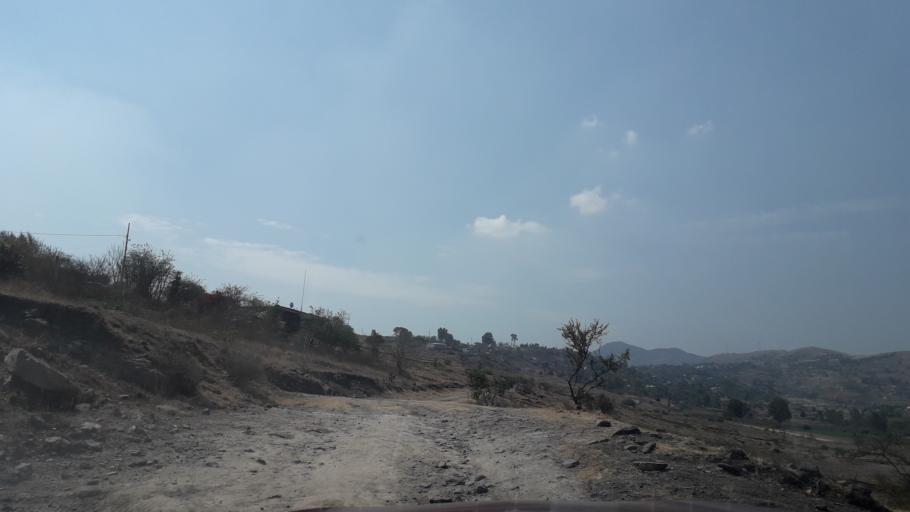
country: MX
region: Puebla
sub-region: Puebla
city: San Andres Azumiatla
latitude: 18.9160
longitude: -98.2597
